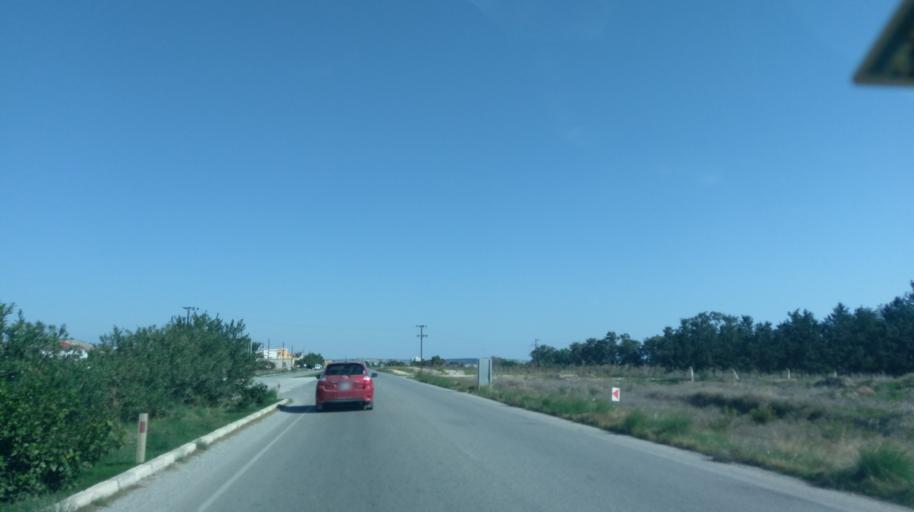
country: CY
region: Ammochostos
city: Trikomo
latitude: 35.3192
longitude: 33.9581
